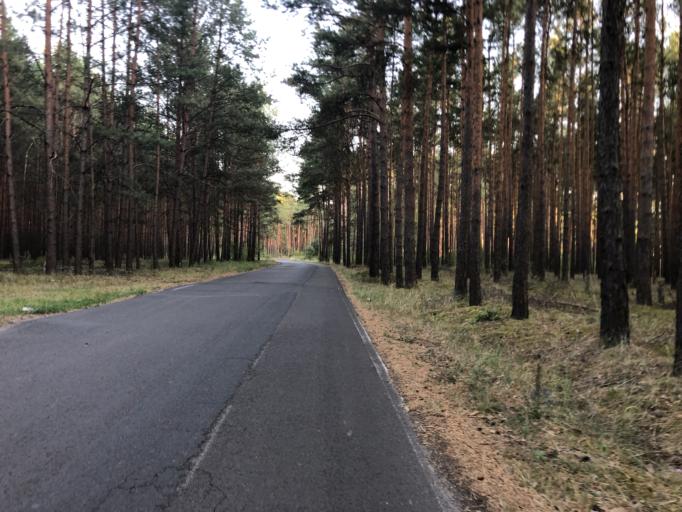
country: DE
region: Brandenburg
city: Gross Lindow
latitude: 52.2574
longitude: 14.4778
